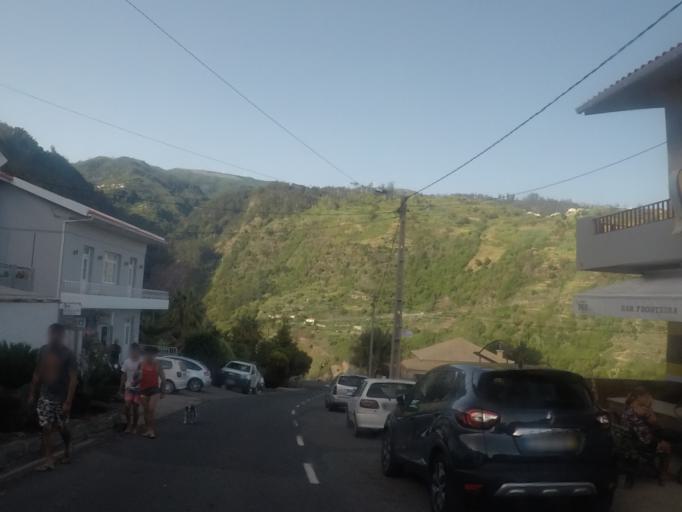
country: PT
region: Madeira
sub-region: Calheta
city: Arco da Calheta
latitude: 32.7074
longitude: -17.1384
